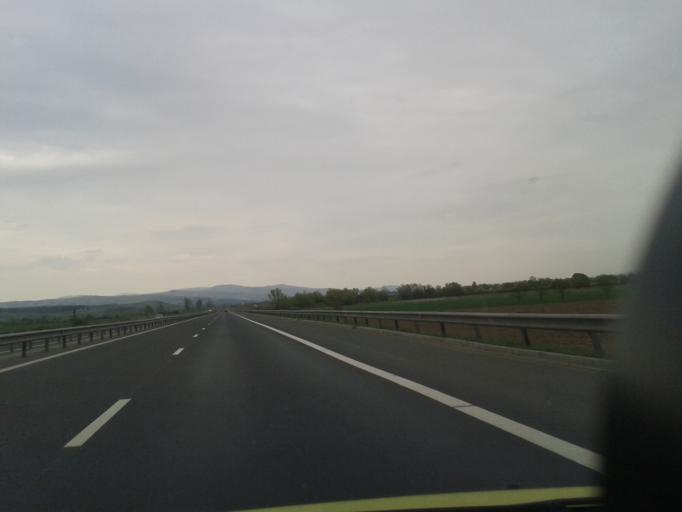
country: RO
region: Hunedoara
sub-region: Comuna Turdas
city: Pricaz
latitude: 45.8594
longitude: 23.1470
